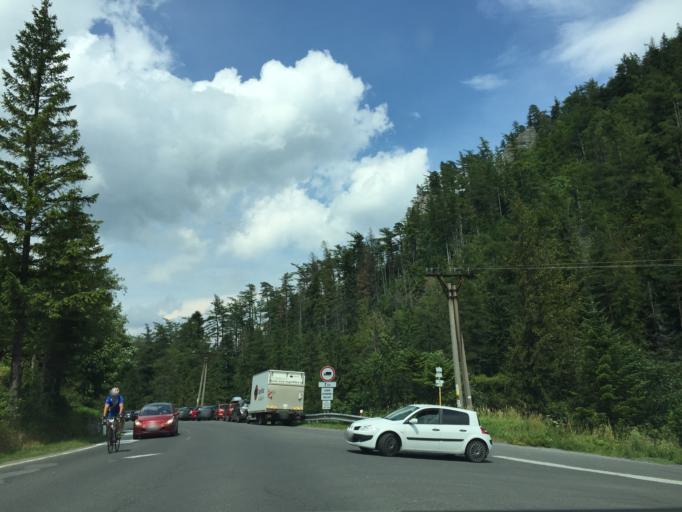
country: SK
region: Presovsky
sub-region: Okres Poprad
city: Zdiar
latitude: 49.2309
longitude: 20.3159
